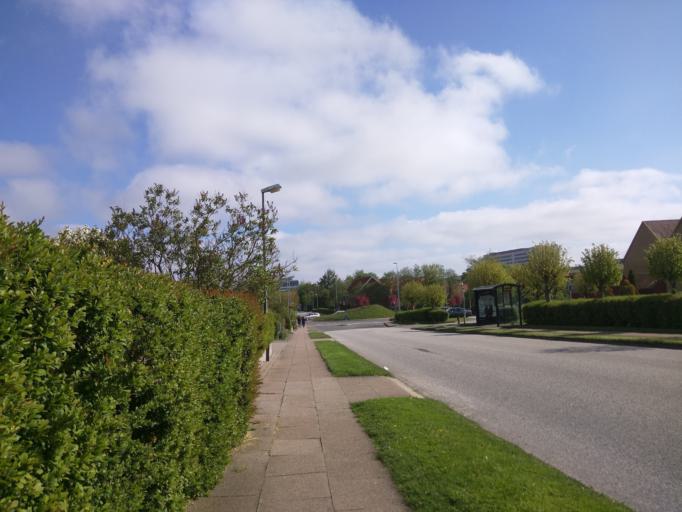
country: DK
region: Central Jutland
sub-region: Viborg Kommune
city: Viborg
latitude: 56.4418
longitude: 9.3965
